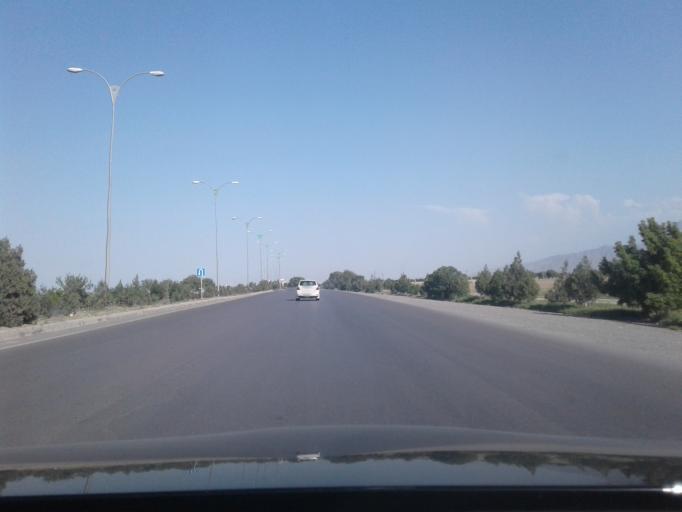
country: TM
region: Ahal
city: Abadan
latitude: 38.1384
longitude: 58.0036
